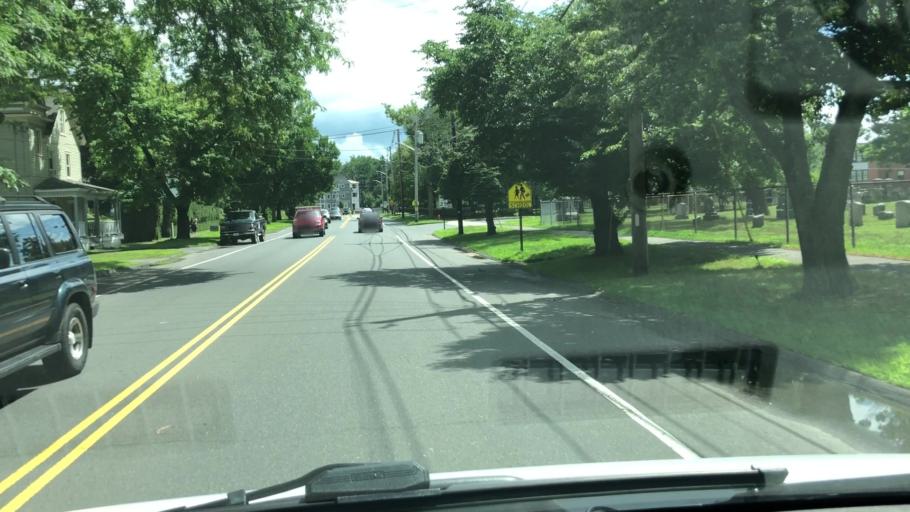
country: US
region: Massachusetts
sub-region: Hampshire County
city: Northampton
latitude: 42.3252
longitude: -72.6252
